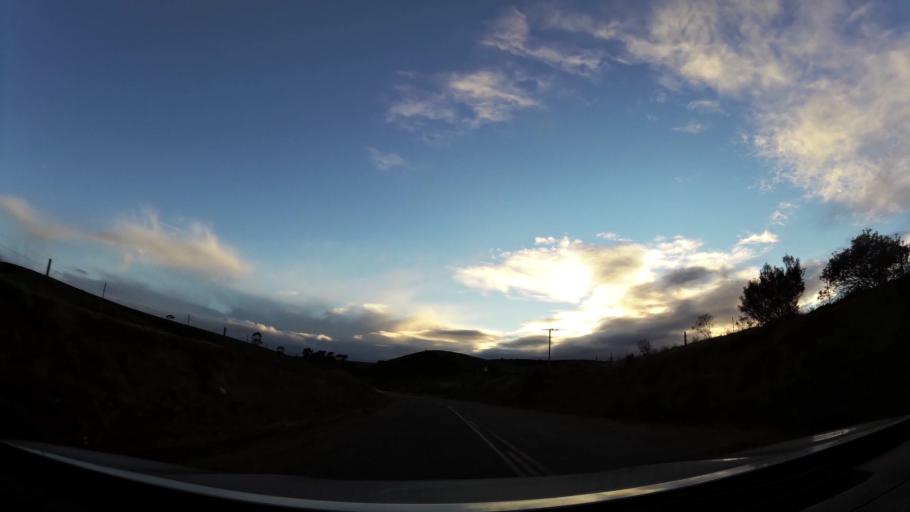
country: ZA
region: Western Cape
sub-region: Eden District Municipality
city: Riversdale
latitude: -34.0552
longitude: 20.8579
